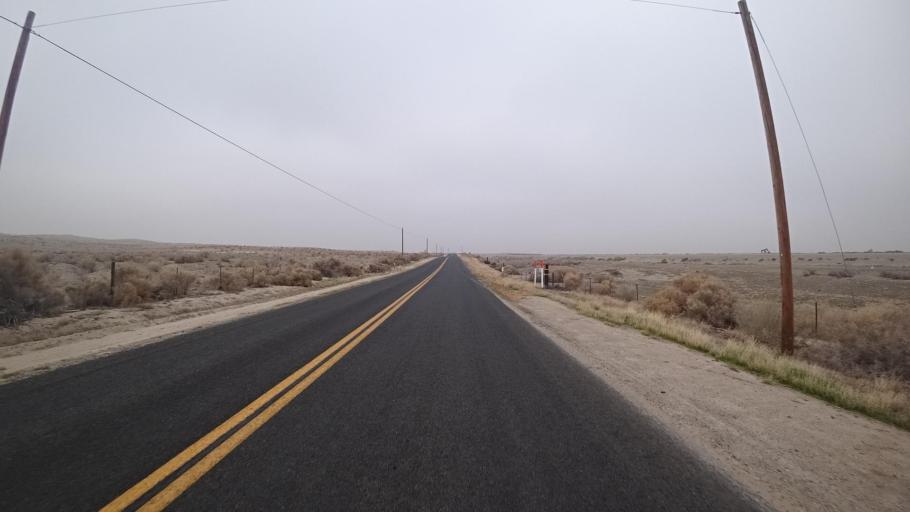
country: US
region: California
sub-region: Kern County
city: Ford City
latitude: 35.2449
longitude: -119.3040
